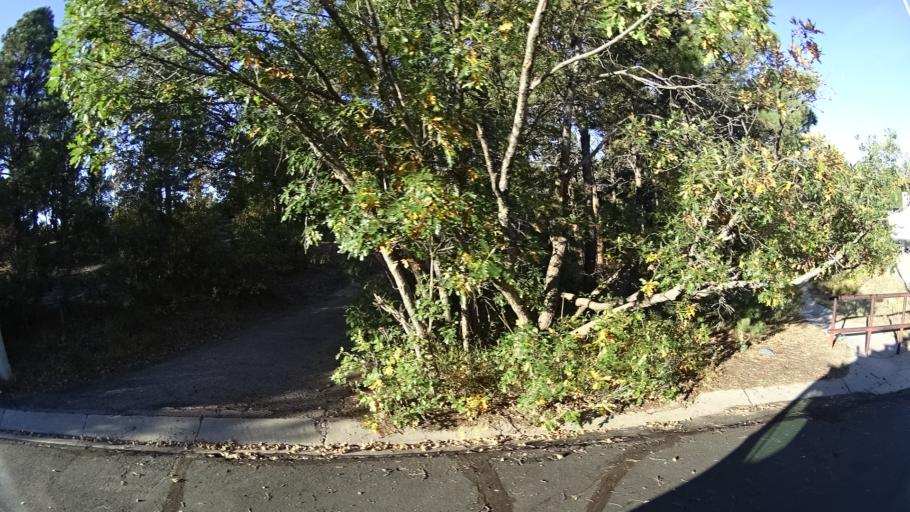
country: US
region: Colorado
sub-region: El Paso County
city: Colorado Springs
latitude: 38.8857
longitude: -104.7686
